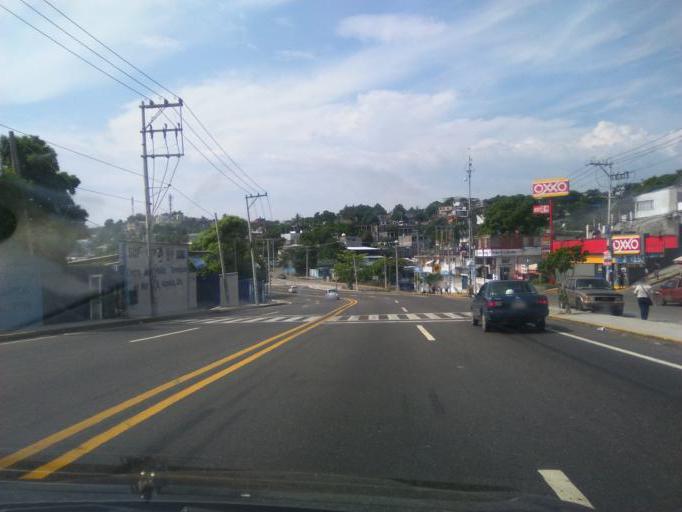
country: MX
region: Guerrero
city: Acapulco de Juarez
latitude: 16.8820
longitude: -99.9484
